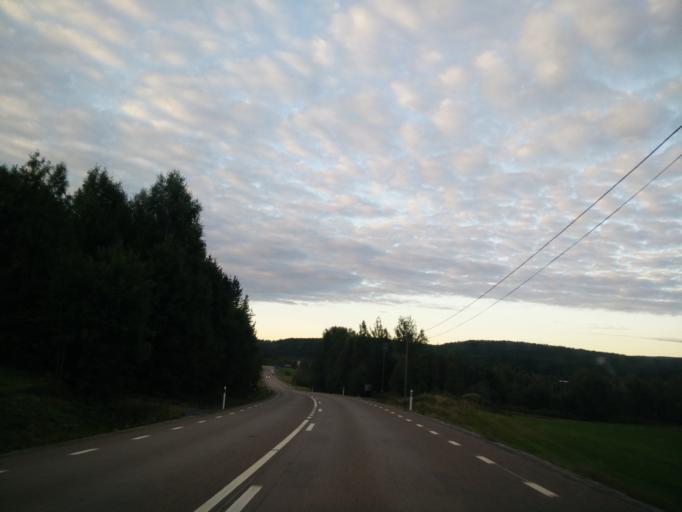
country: SE
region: Vaesternorrland
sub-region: Kramfors Kommun
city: Nordingra
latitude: 62.9249
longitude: 18.0800
